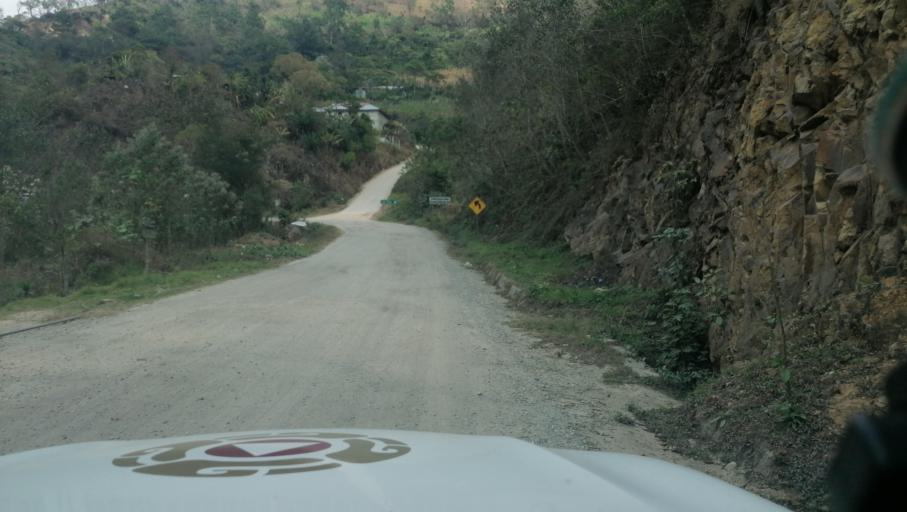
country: GT
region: San Marcos
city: Tacana
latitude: 15.2161
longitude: -92.2023
